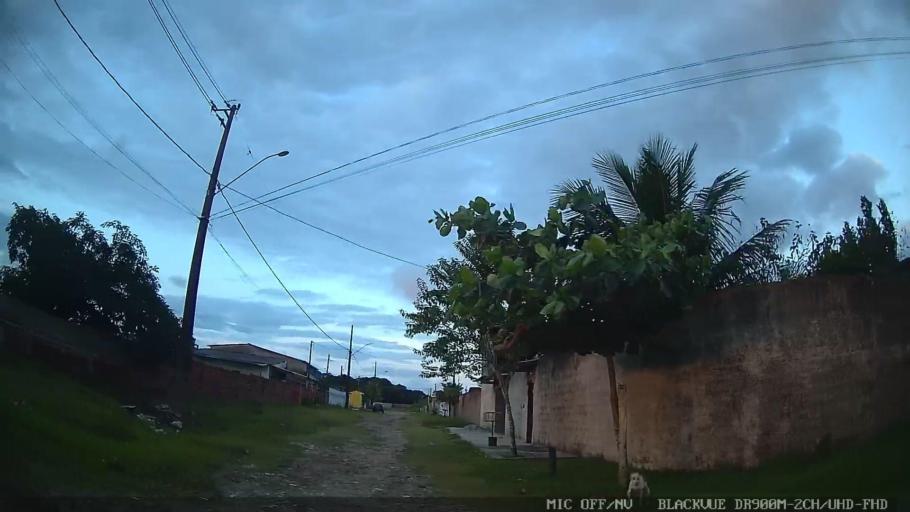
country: BR
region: Sao Paulo
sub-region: Itanhaem
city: Itanhaem
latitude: -24.1843
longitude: -46.8348
